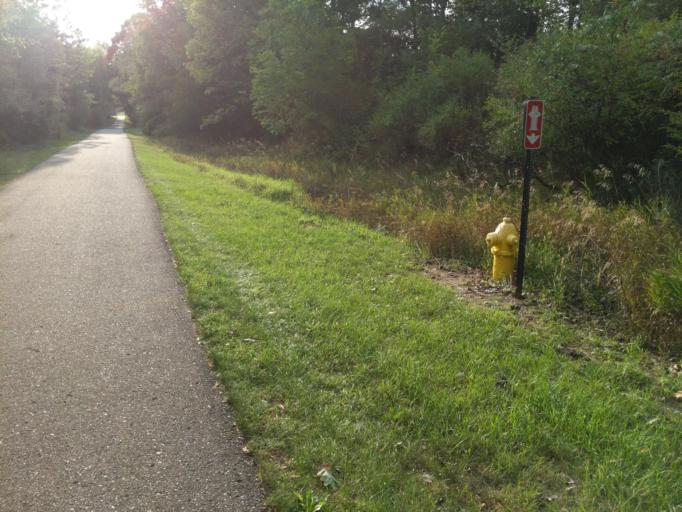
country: US
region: Michigan
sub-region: Ionia County
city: Portland
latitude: 42.8836
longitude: -84.9200
